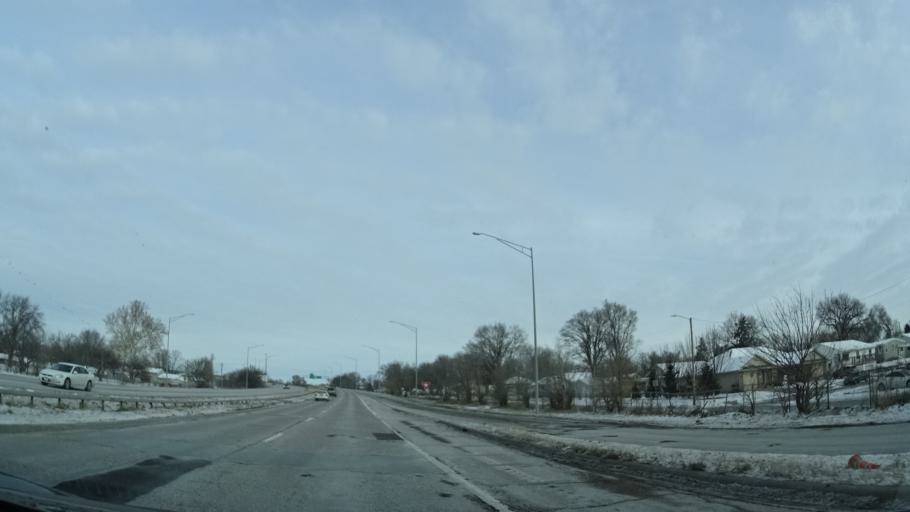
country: US
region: Nebraska
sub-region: Douglas County
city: Omaha
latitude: 41.2558
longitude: -95.9067
